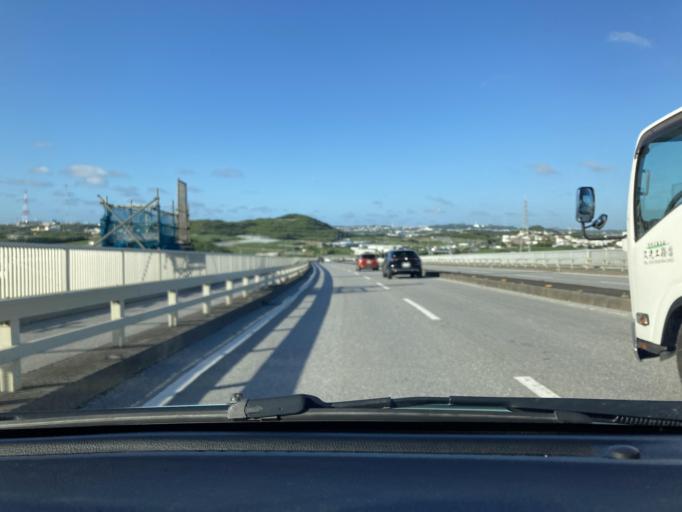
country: JP
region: Okinawa
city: Tomigusuku
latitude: 26.1664
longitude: 127.7077
